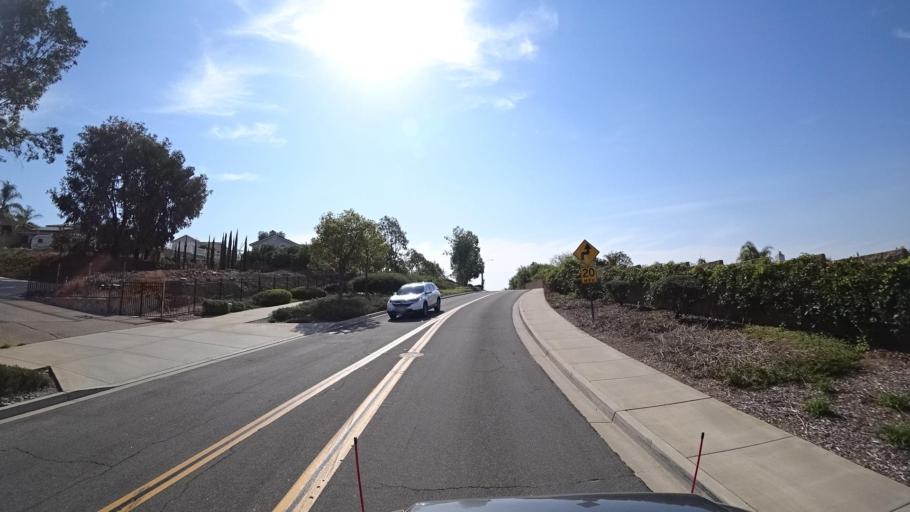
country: US
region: California
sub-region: San Diego County
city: San Marcos
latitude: 33.1565
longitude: -117.1448
